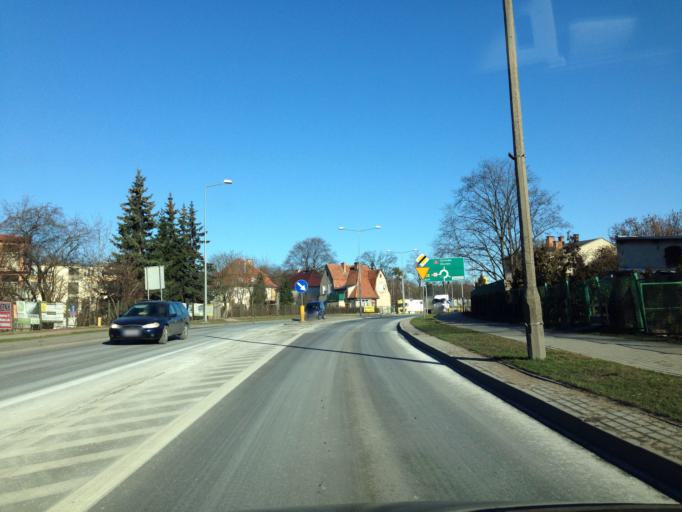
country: PL
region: Warmian-Masurian Voivodeship
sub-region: Powiat nowomiejski
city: Nowe Miasto Lubawskie
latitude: 53.4243
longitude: 19.5888
